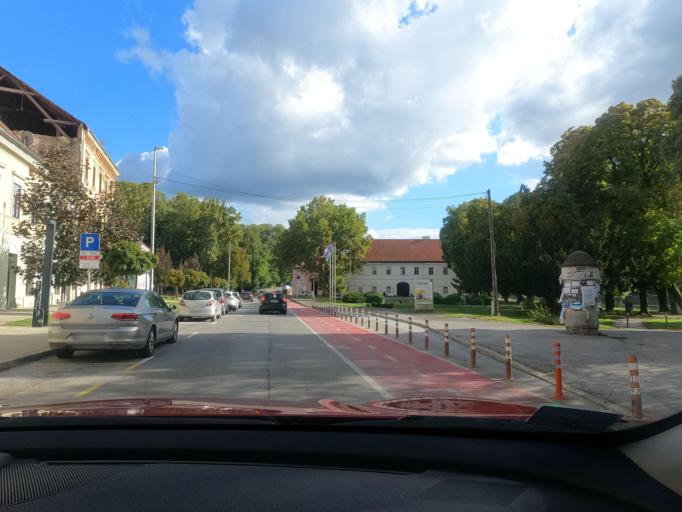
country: HR
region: Sisacko-Moslavacka
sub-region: Grad Sisak
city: Sisak
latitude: 45.4850
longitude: 16.3710
